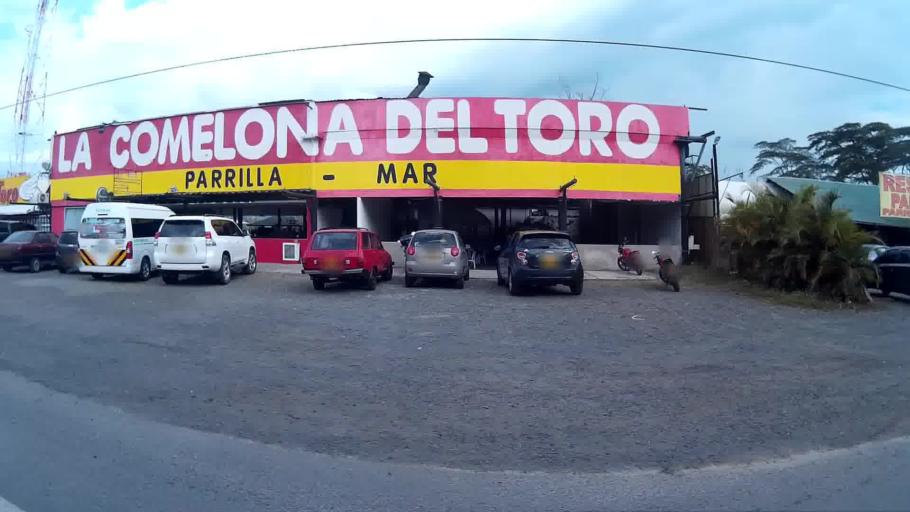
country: CO
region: Valle del Cauca
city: Cartago
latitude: 4.8067
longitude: -75.8159
